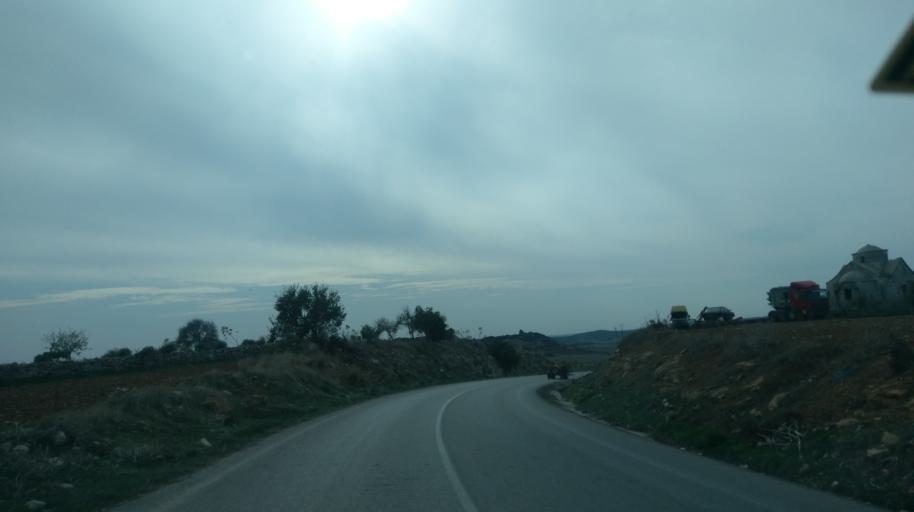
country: CY
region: Ammochostos
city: Leonarisso
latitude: 35.4693
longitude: 34.1454
